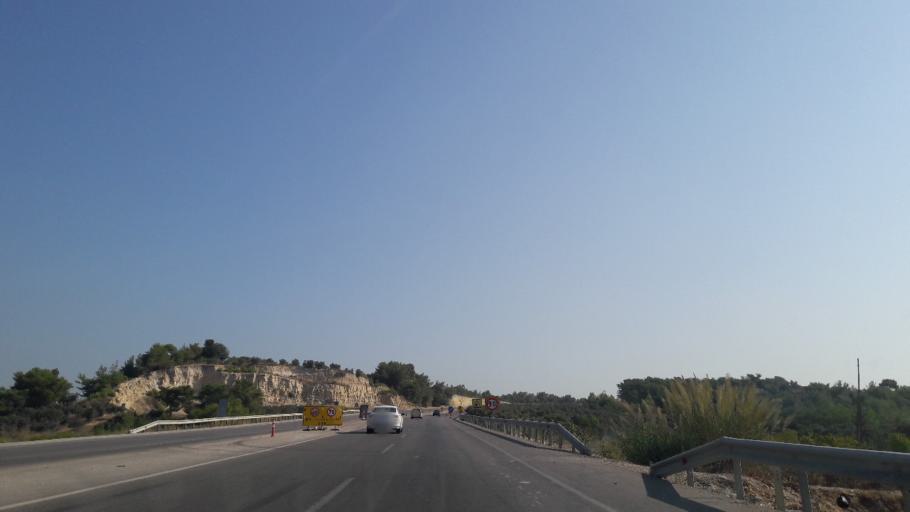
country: TR
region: Adana
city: Yuregir
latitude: 37.0782
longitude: 35.4728
